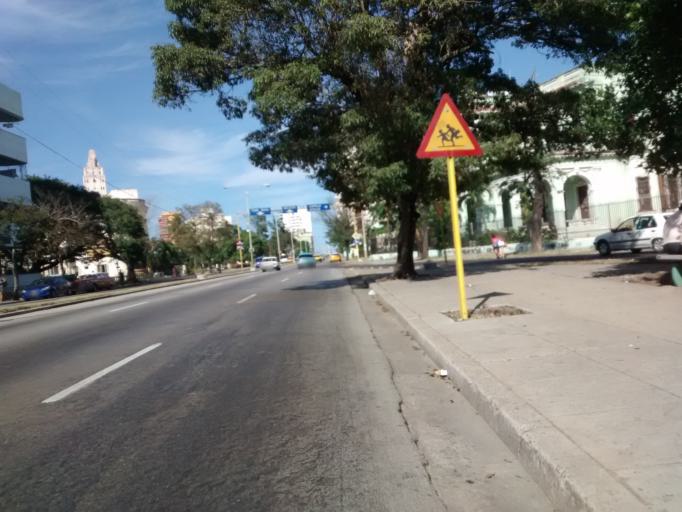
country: CU
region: La Habana
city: Havana
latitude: 23.1423
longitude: -82.3896
